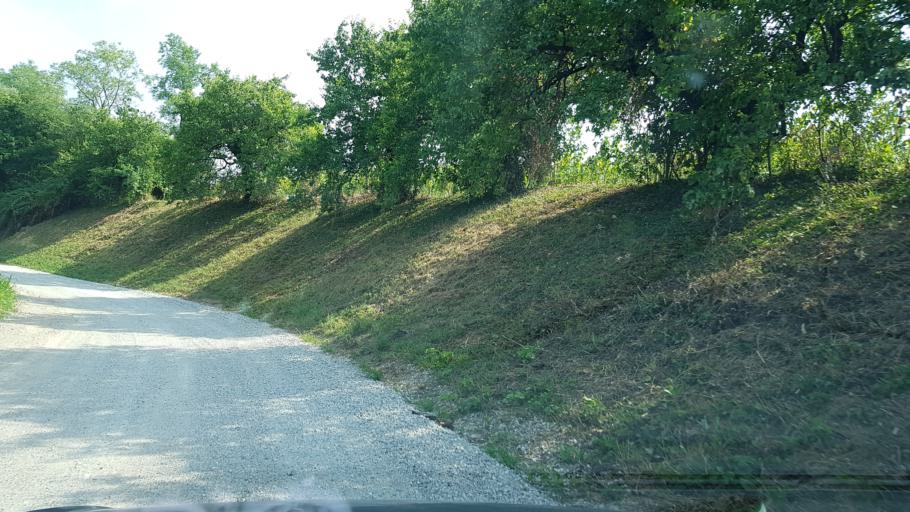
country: SI
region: Brda
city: Dobrovo
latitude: 45.9965
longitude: 13.5140
